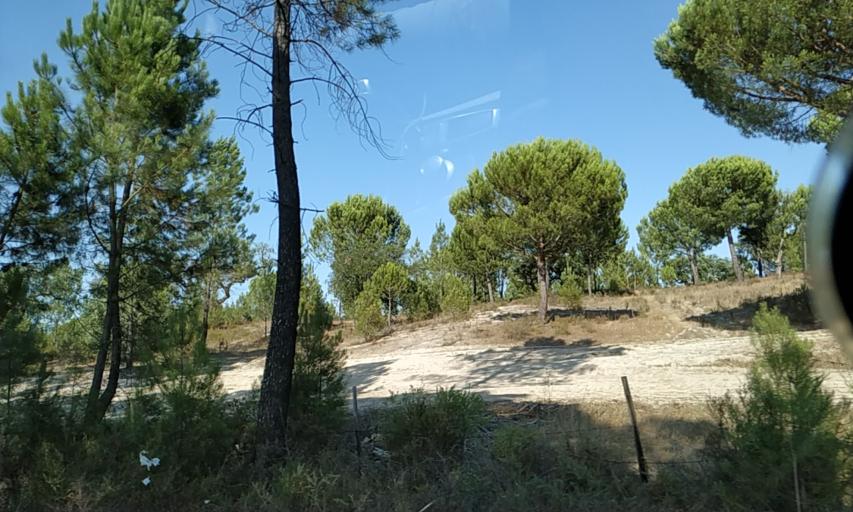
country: PT
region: Santarem
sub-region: Coruche
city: Coruche
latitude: 38.8952
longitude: -8.5339
